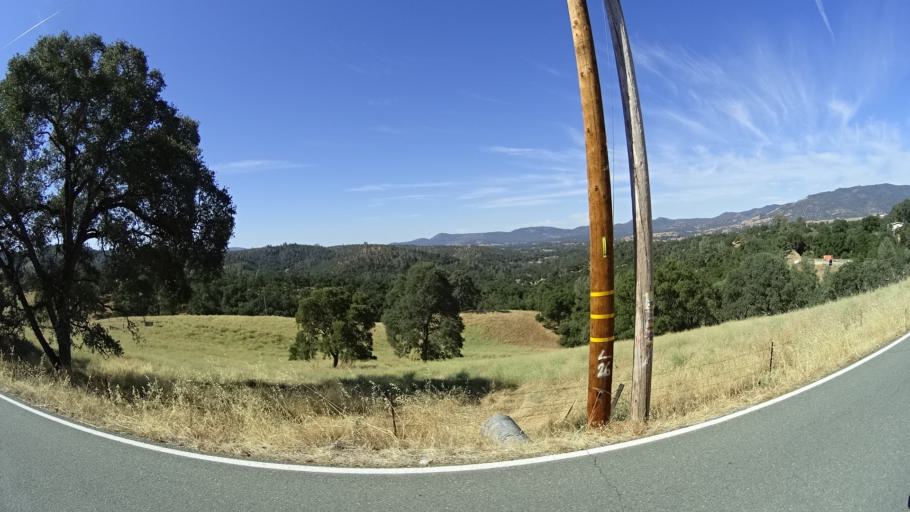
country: US
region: California
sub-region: Calaveras County
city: San Andreas
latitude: 38.1492
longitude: -120.6105
